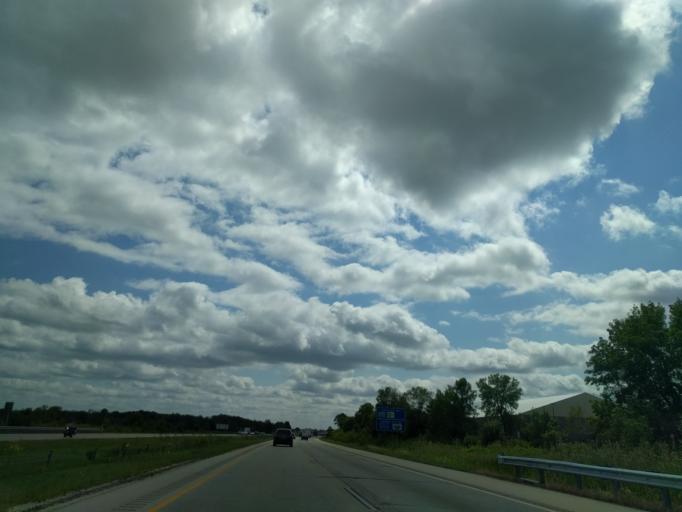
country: US
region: Wisconsin
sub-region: Milwaukee County
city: Bayside
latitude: 43.2313
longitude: -87.9201
